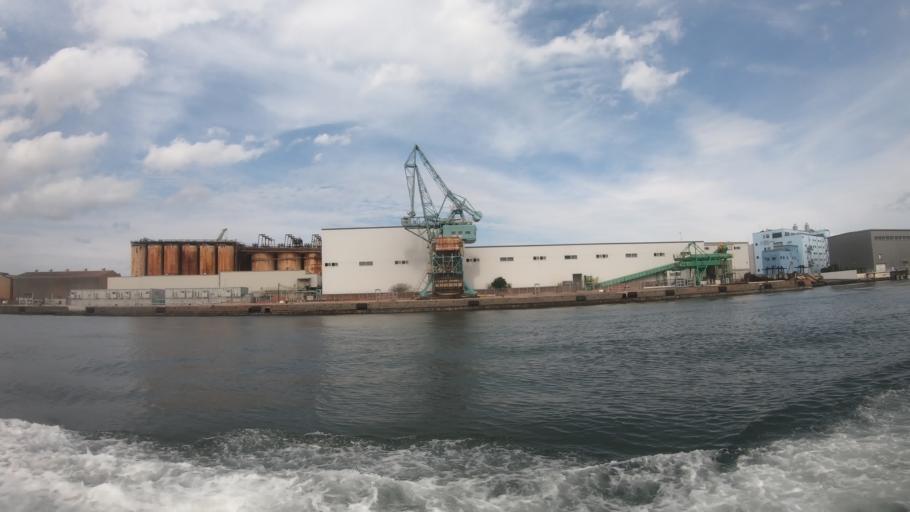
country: JP
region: Kanagawa
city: Yokohama
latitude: 35.4757
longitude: 139.6587
